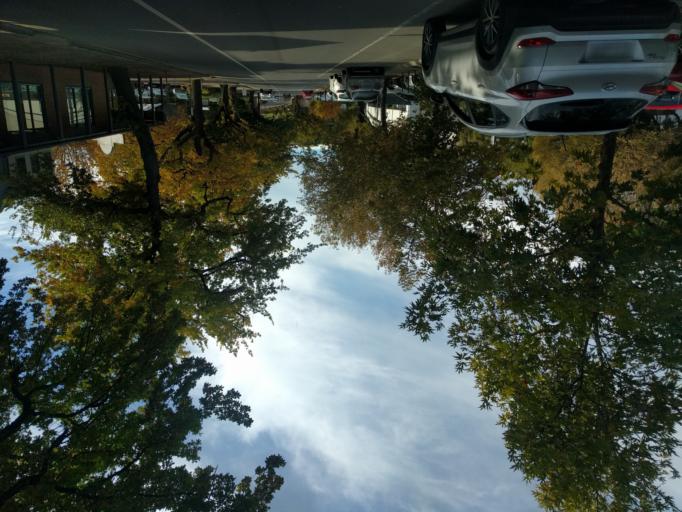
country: AU
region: South Australia
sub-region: Mount Barker
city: Mount Barker
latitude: -35.0683
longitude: 138.8595
